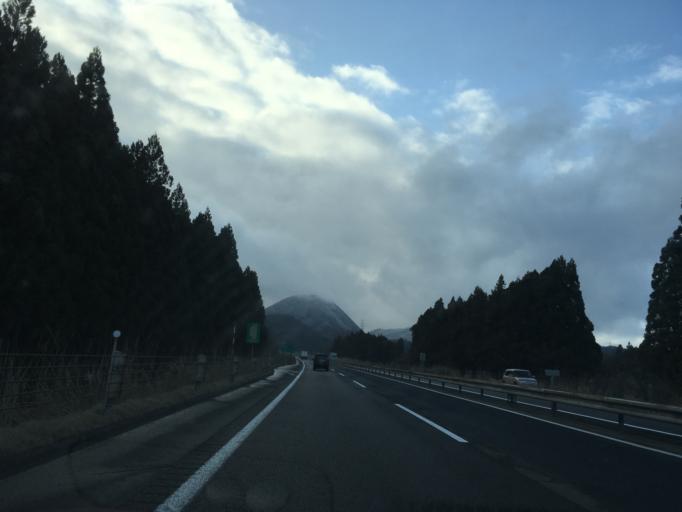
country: JP
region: Miyagi
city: Shiroishi
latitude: 38.1799
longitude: 140.6096
